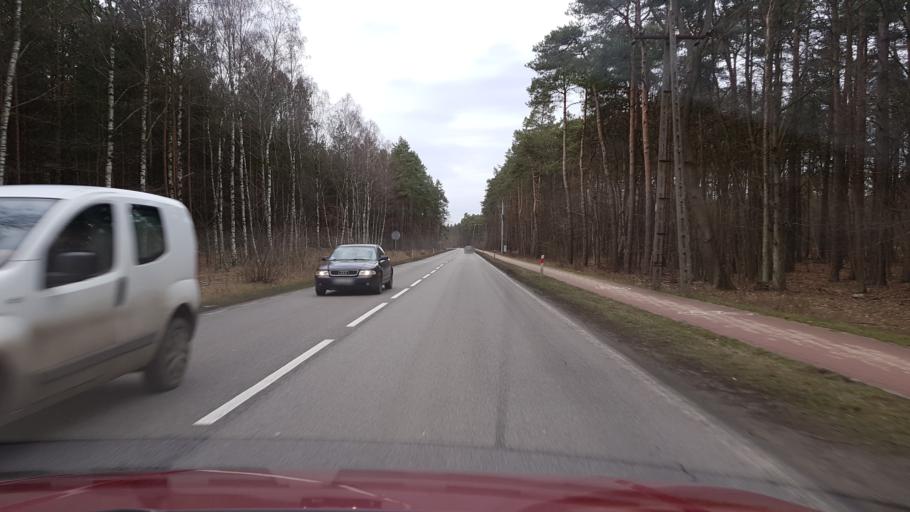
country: PL
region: West Pomeranian Voivodeship
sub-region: Powiat policki
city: Dobra
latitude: 53.5051
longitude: 14.4774
